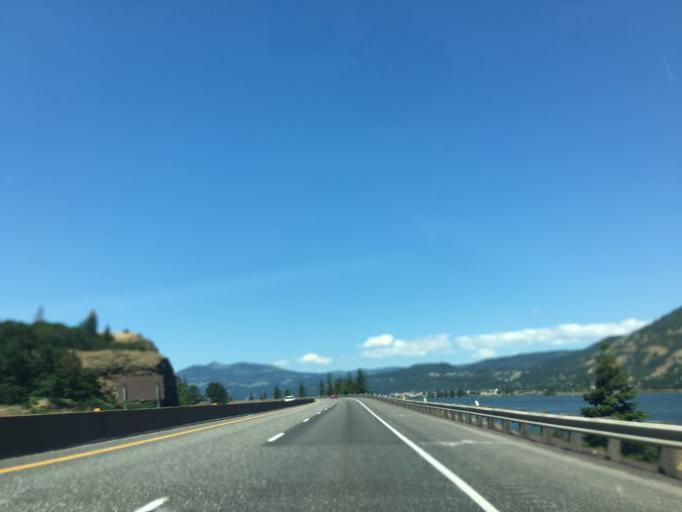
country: US
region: Washington
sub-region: Klickitat County
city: White Salmon
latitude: 45.6941
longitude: -121.4443
